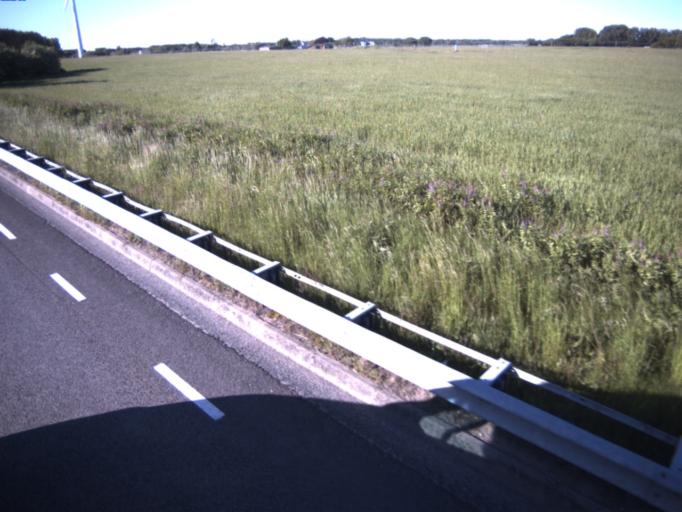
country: SE
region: Skane
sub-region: Helsingborg
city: Rydeback
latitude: 55.9905
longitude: 12.7638
